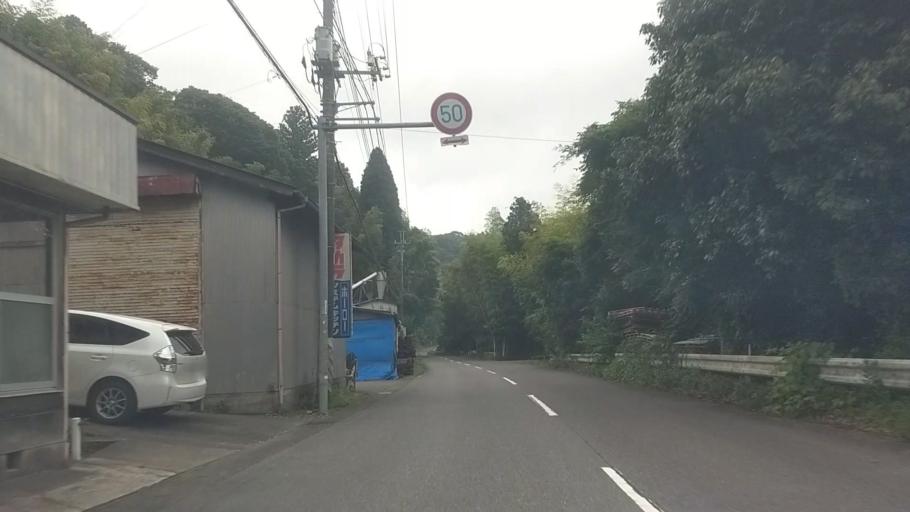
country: JP
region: Chiba
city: Katsuura
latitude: 35.2432
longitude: 140.2427
